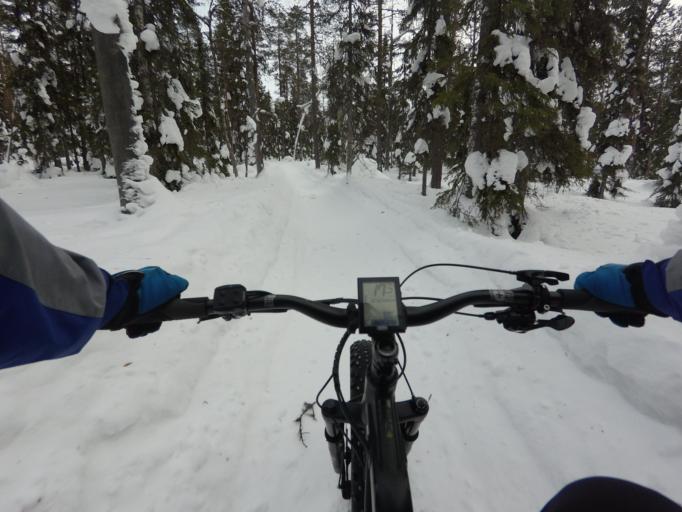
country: FI
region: Lapland
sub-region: Tunturi-Lappi
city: Kolari
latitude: 67.5986
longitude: 24.2741
